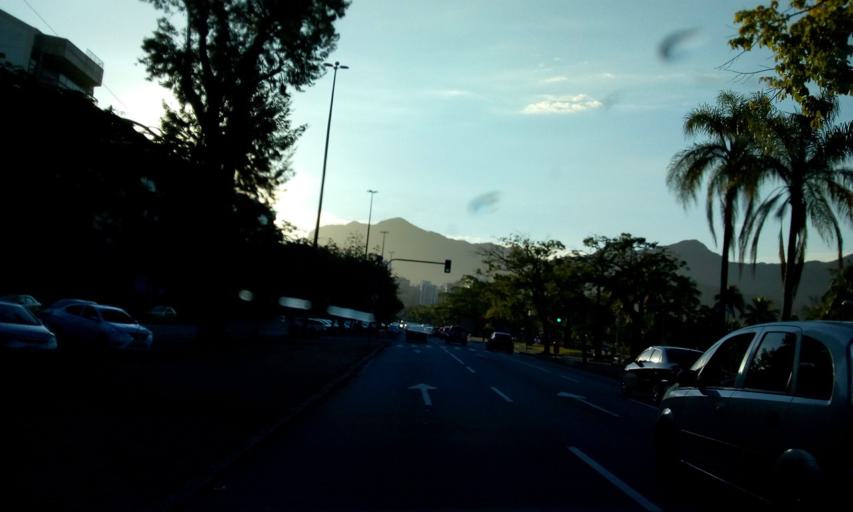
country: BR
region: Rio de Janeiro
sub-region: Rio De Janeiro
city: Rio de Janeiro
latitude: -22.9805
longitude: -43.2107
